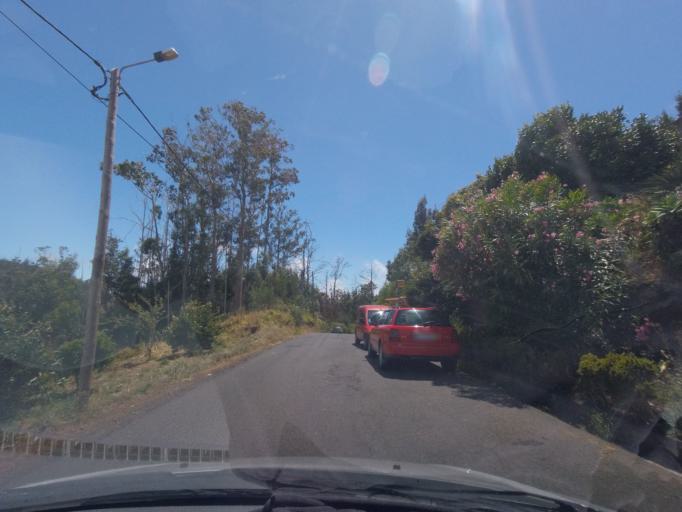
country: PT
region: Madeira
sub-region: Santa Cruz
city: Camacha
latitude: 32.6939
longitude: -16.8371
